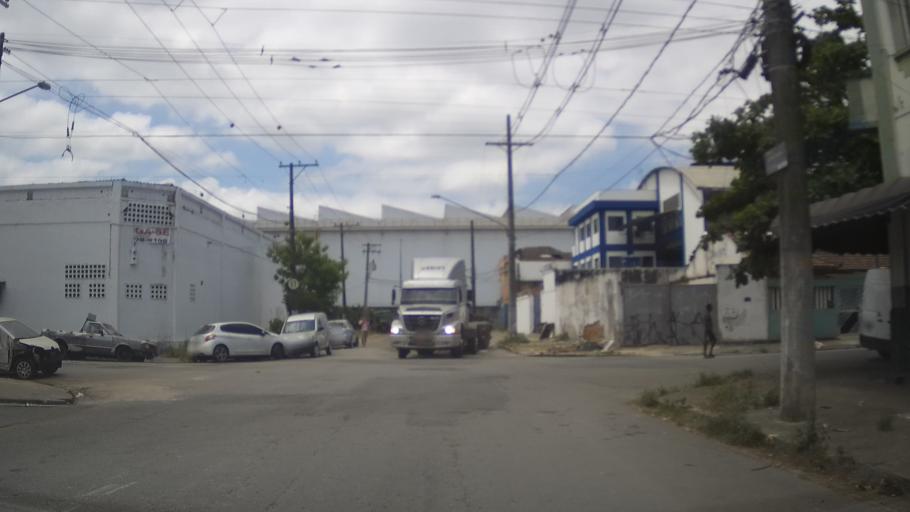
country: BR
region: Sao Paulo
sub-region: Santos
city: Santos
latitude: -23.9525
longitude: -46.3144
